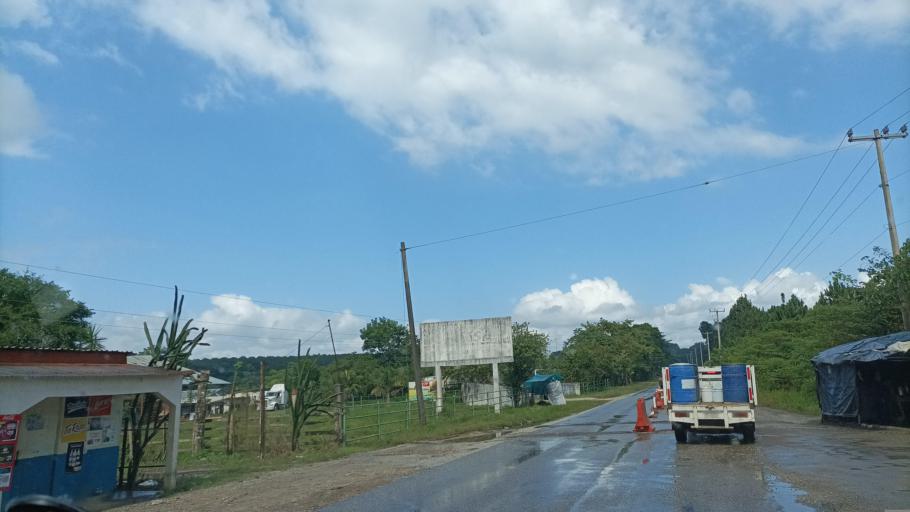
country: MX
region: Veracruz
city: Las Choapas
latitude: 17.8556
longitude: -94.1029
